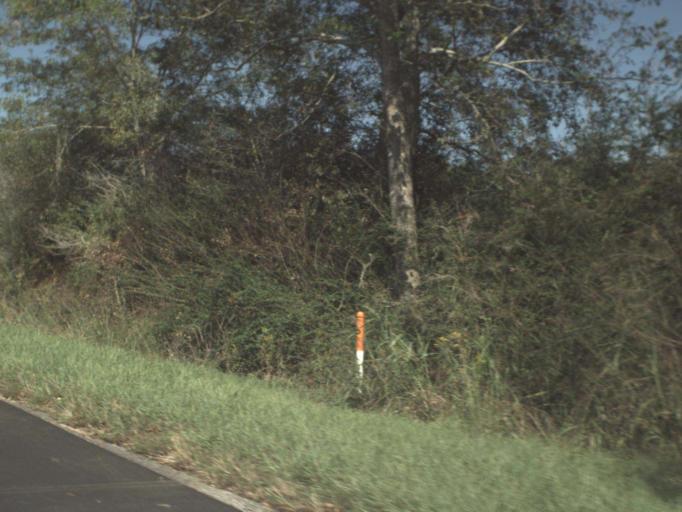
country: US
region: Alabama
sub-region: Covington County
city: Florala
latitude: 30.9522
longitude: -86.2901
